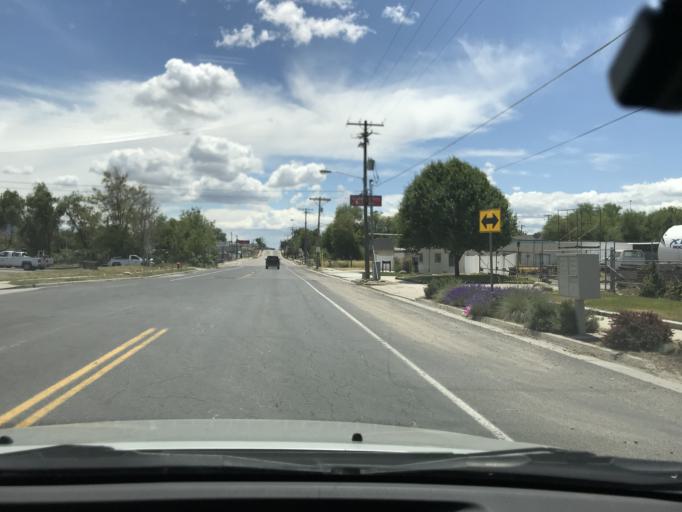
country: US
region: Utah
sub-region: Salt Lake County
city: Centerfield
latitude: 40.6820
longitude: -111.8998
